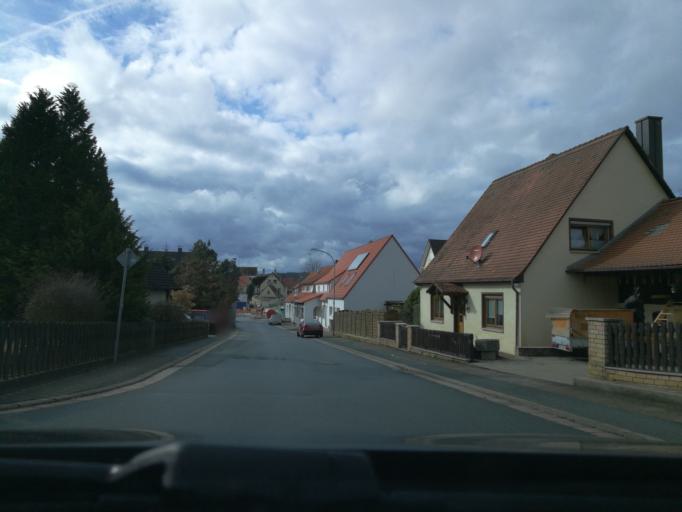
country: DE
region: Bavaria
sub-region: Regierungsbezirk Mittelfranken
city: Rottenbach
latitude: 49.6676
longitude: 10.9286
